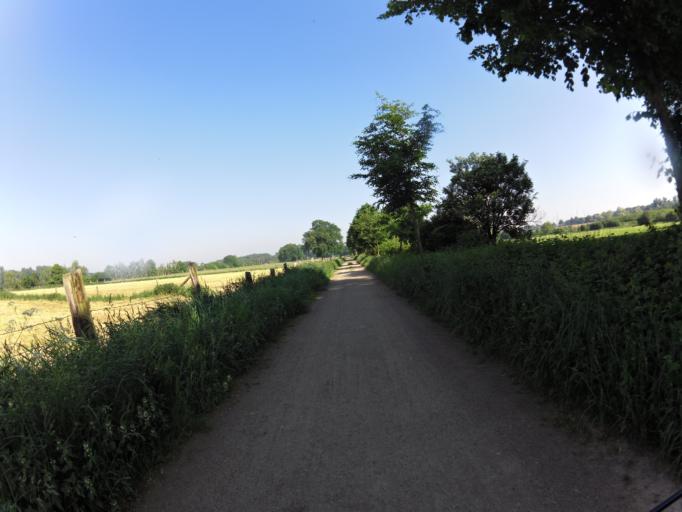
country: DE
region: North Rhine-Westphalia
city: Julich
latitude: 50.9529
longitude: 6.3220
